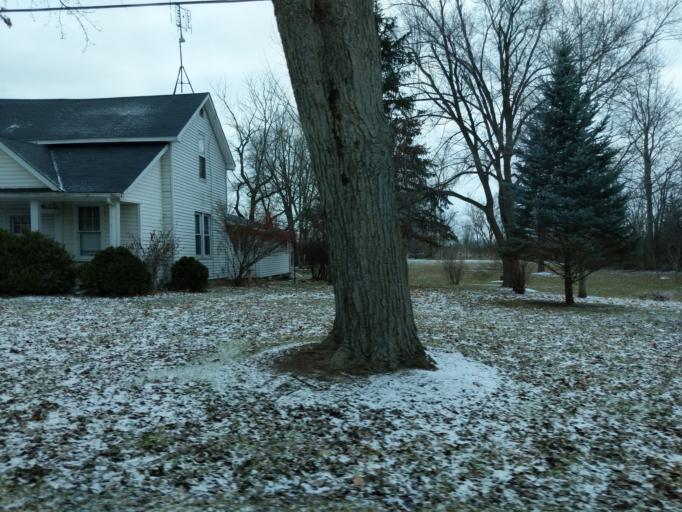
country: US
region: Michigan
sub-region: Sanilac County
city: Marlette
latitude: 43.3278
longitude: -83.0881
